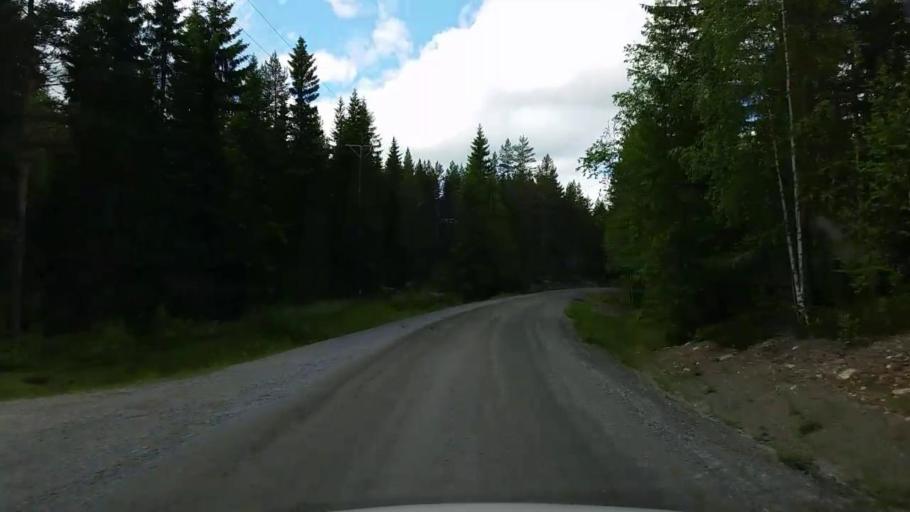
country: SE
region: Gaevleborg
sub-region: Bollnas Kommun
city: Vittsjo
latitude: 61.0683
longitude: 16.2849
